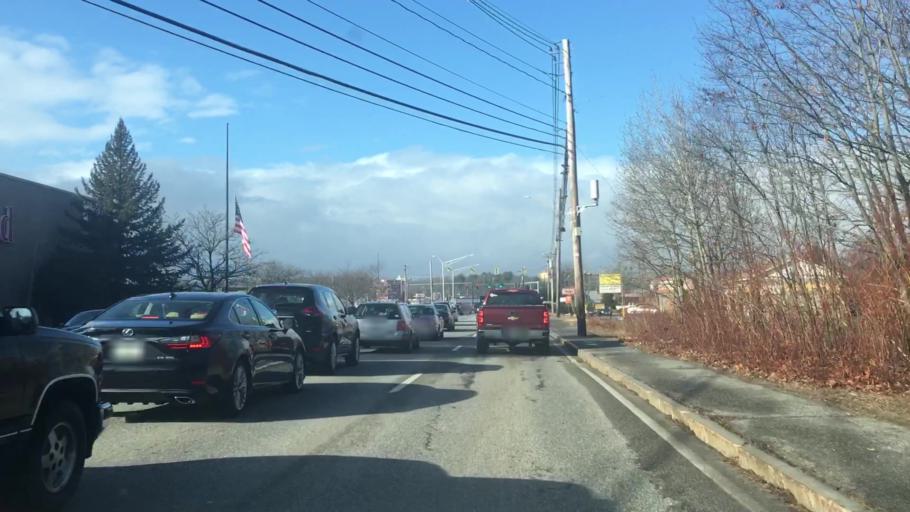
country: US
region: Maine
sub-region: Cumberland County
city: South Portland Gardens
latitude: 43.6350
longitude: -70.3276
